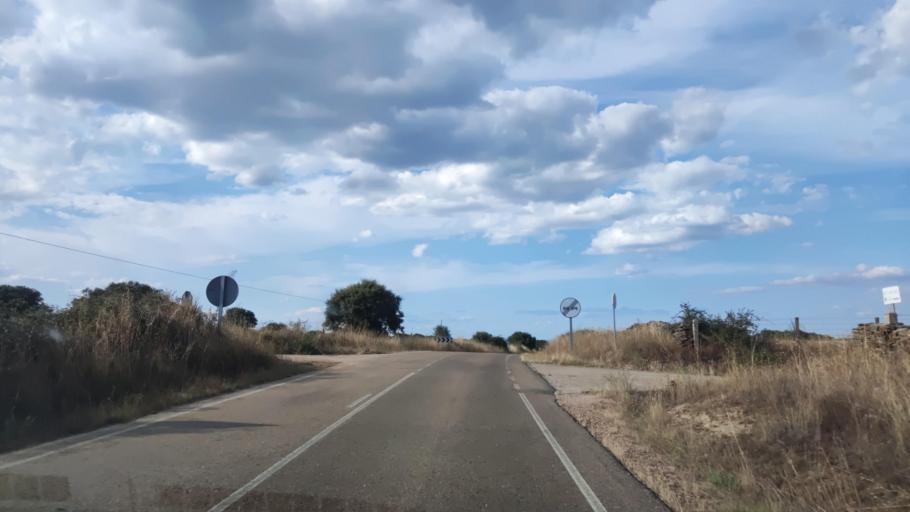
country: ES
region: Castille and Leon
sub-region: Provincia de Salamanca
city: Martiago
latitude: 40.4620
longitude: -6.4902
